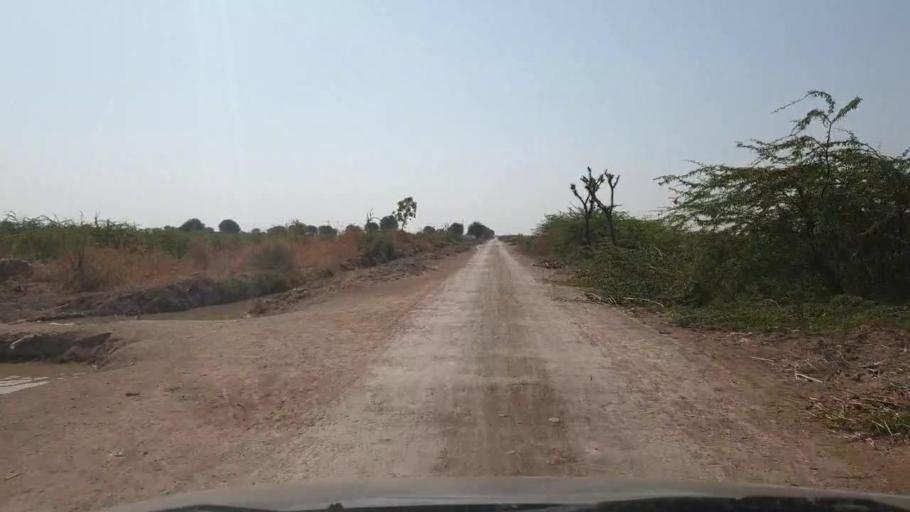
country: PK
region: Sindh
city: Digri
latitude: 25.2010
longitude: 69.2282
